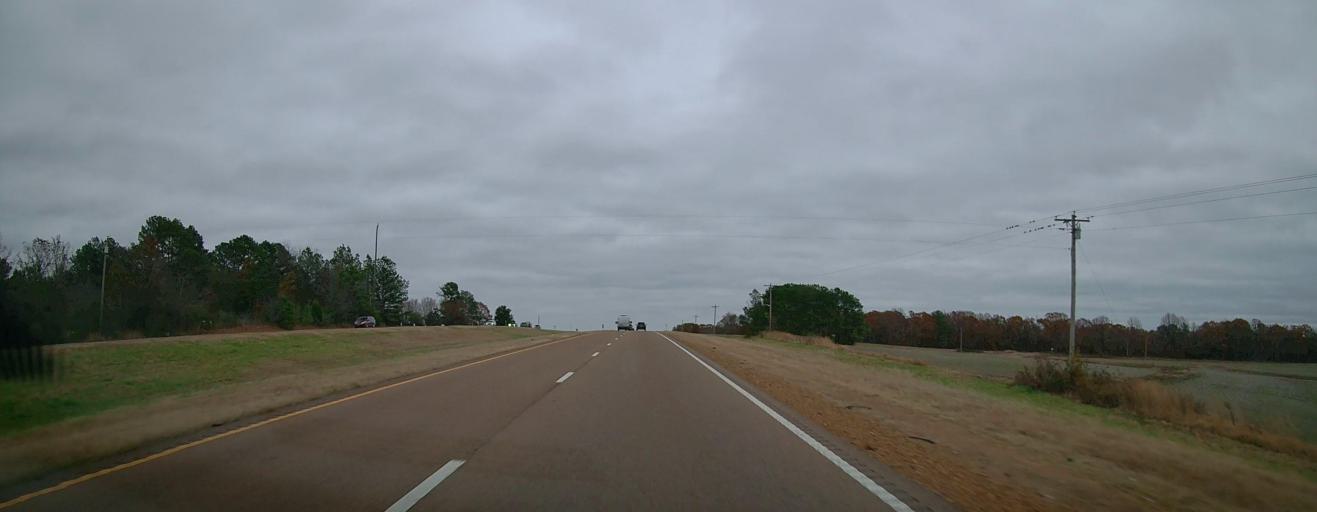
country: US
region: Mississippi
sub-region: Benton County
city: Ashland
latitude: 34.9461
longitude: -89.3209
